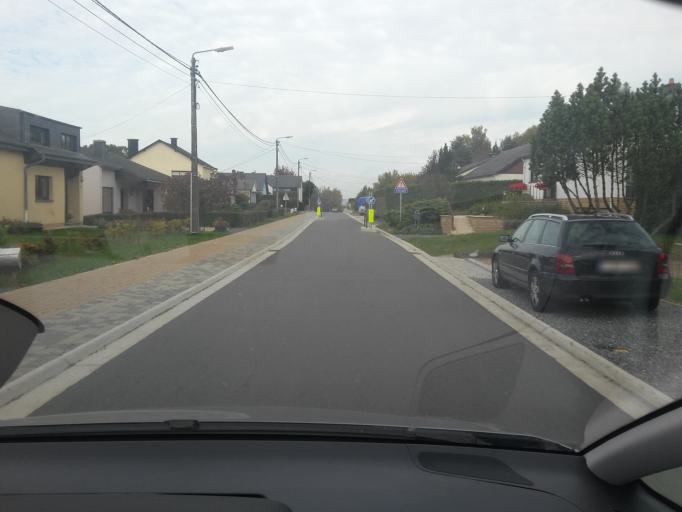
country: BE
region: Wallonia
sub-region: Province du Luxembourg
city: Arlon
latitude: 49.7019
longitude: 5.8194
